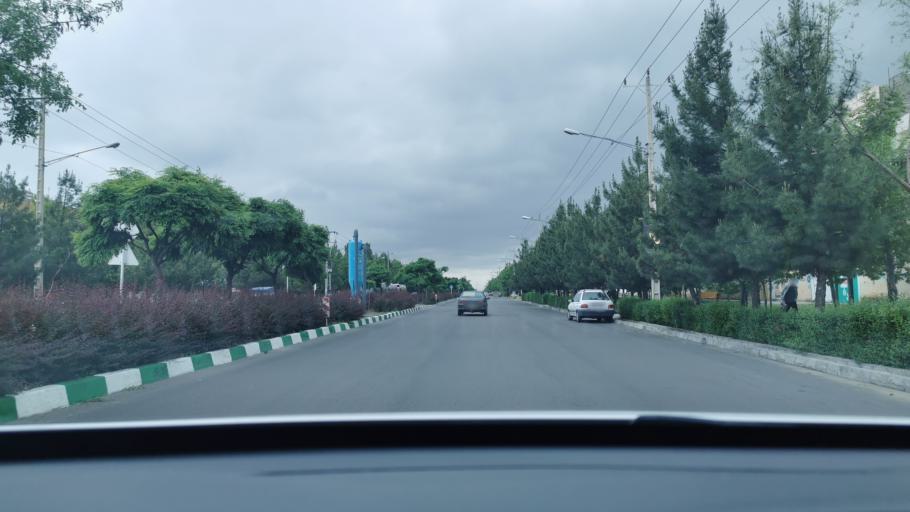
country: IR
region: Razavi Khorasan
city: Mashhad
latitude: 36.3732
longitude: 59.5050
